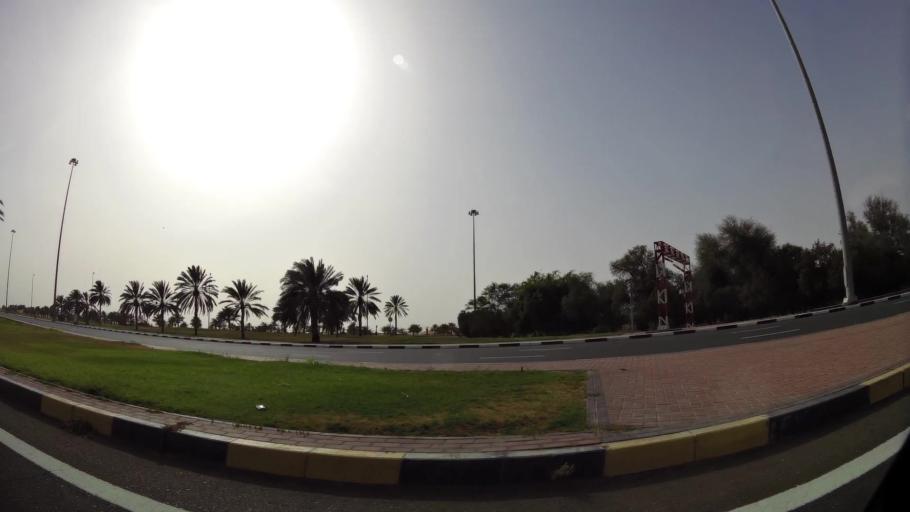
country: AE
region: Abu Dhabi
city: Al Ain
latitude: 24.1830
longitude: 55.5933
